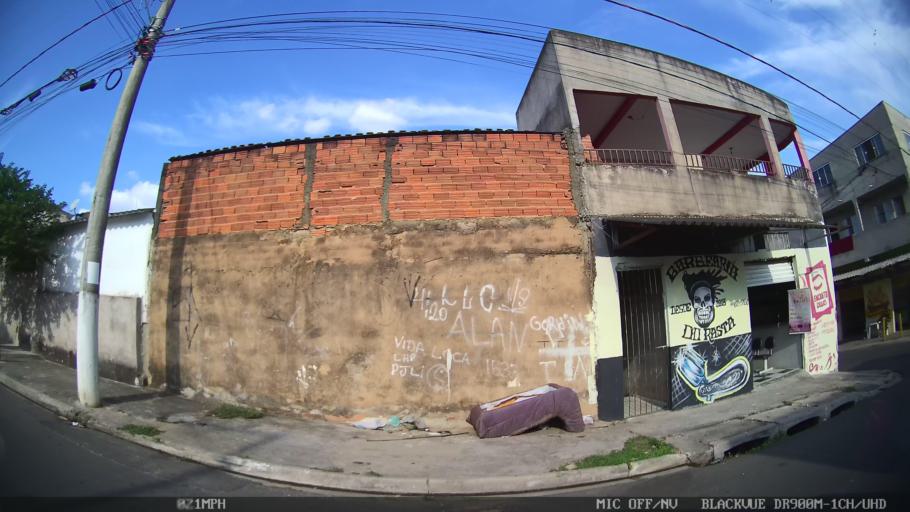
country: BR
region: Sao Paulo
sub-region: Hortolandia
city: Hortolandia
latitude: -22.8543
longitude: -47.1992
